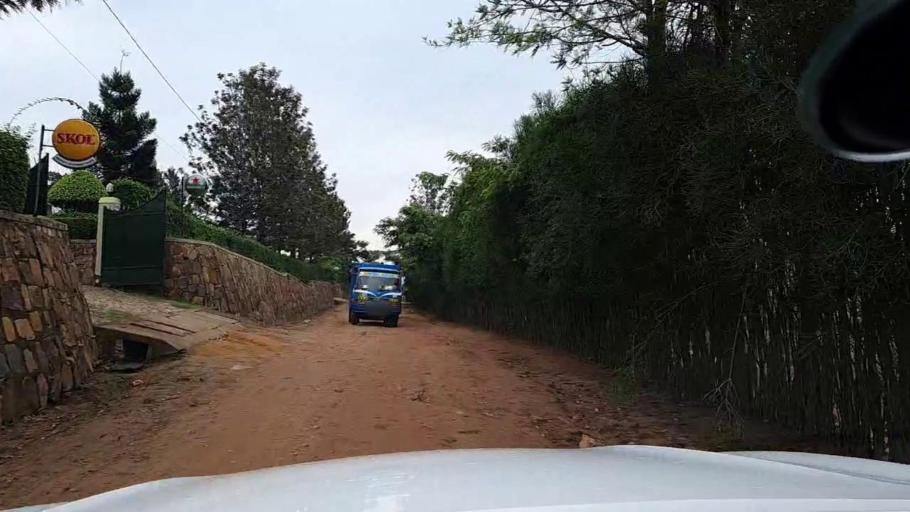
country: RW
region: Kigali
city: Kigali
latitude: -1.9591
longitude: 29.9962
